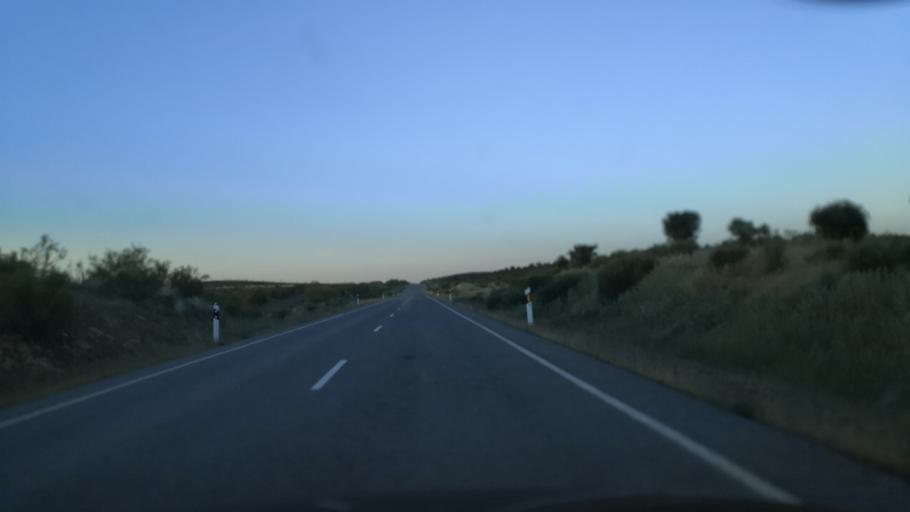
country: ES
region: Extremadura
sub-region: Provincia de Caceres
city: Salorino
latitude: 39.5978
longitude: -6.9835
